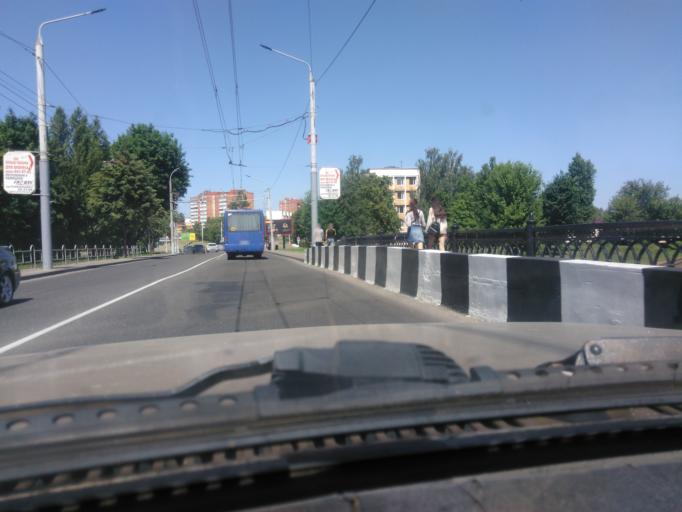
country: BY
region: Mogilev
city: Mahilyow
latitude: 53.9196
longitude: 30.3429
